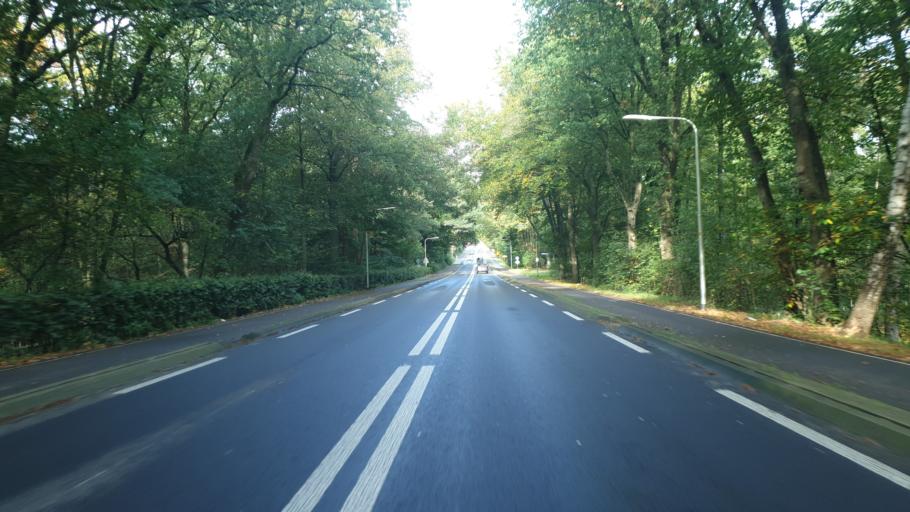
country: NL
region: Gelderland
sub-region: Gemeente Groesbeek
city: Berg en Dal
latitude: 51.8092
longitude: 5.8908
